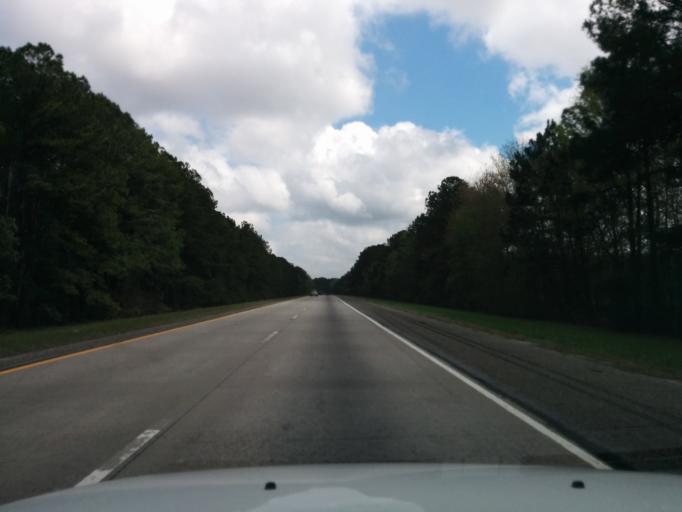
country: US
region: Georgia
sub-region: Bryan County
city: Pembroke
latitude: 32.2287
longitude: -81.6104
